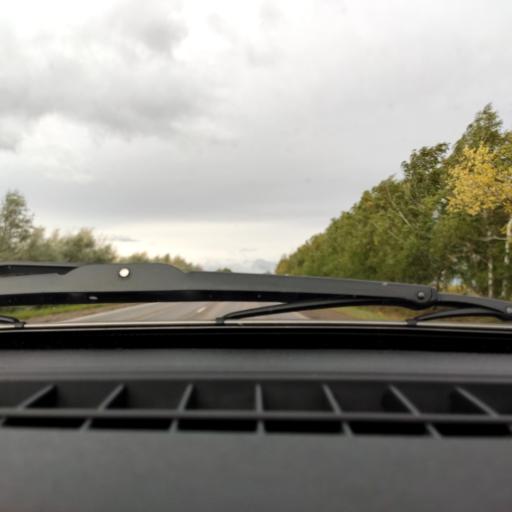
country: RU
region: Bashkortostan
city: Rayevskiy
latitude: 54.1555
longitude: 54.9525
